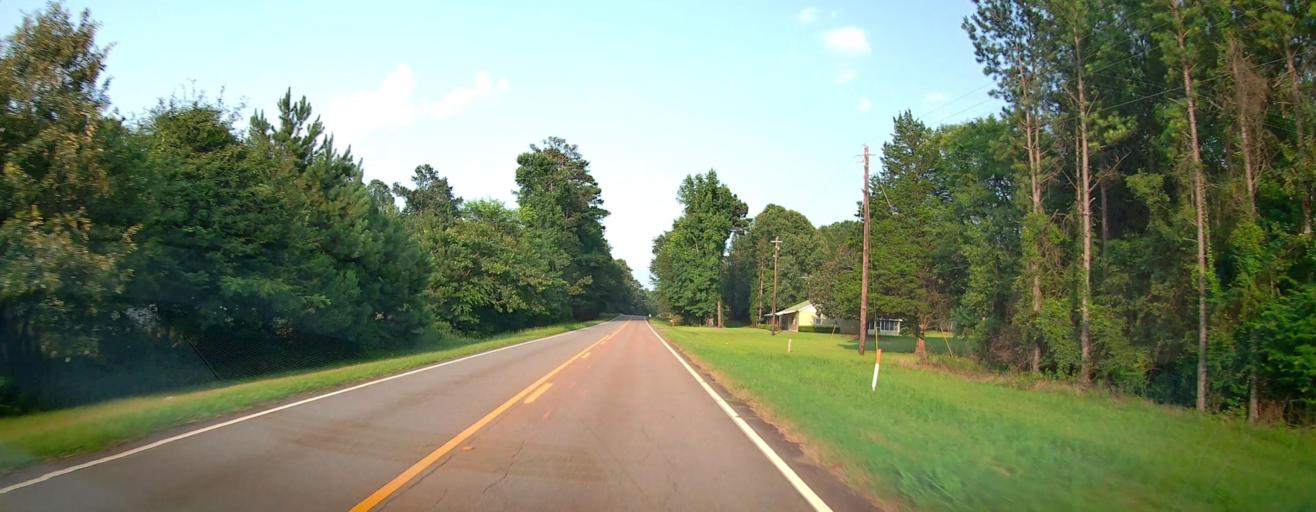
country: US
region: Georgia
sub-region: Jones County
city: Gray
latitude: 33.0596
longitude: -83.5993
